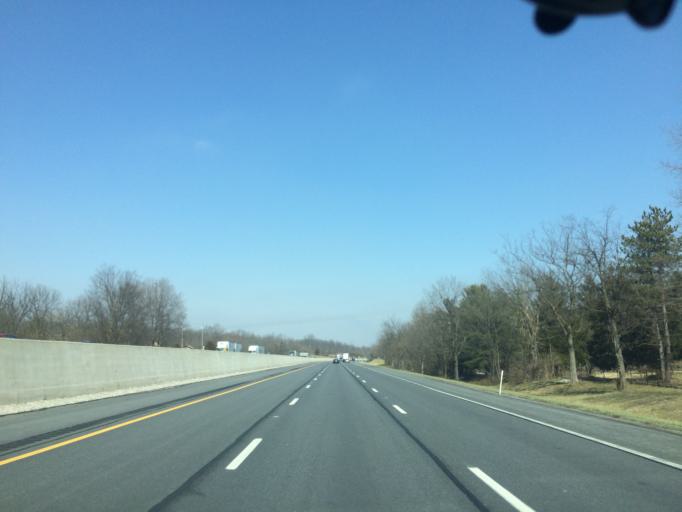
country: US
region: West Virginia
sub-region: Berkeley County
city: Martinsburg
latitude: 39.5199
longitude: -77.9307
